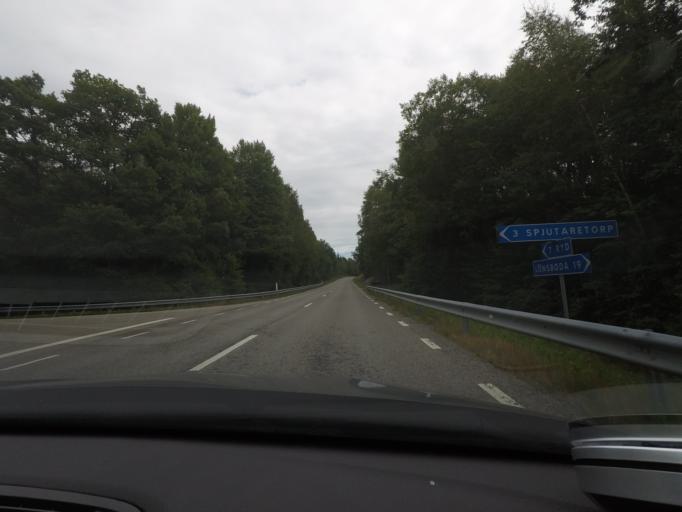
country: SE
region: Blekinge
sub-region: Olofstroms Kommun
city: Olofstroem
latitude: 56.4563
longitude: 14.5855
